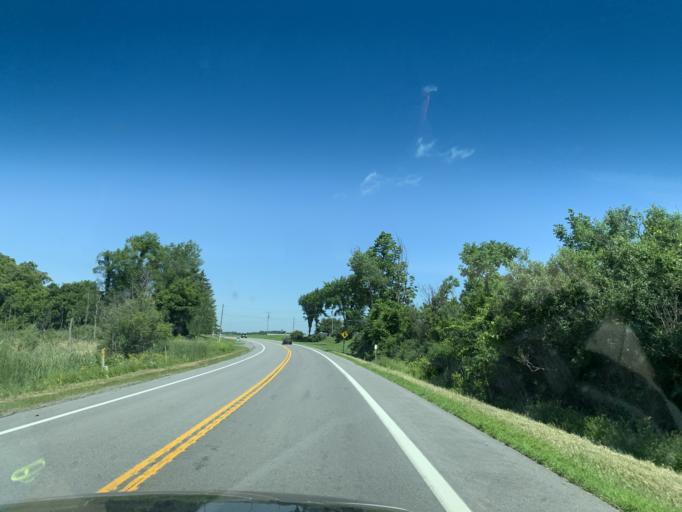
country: US
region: New York
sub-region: Oneida County
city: Chadwicks
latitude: 42.9119
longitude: -75.2399
